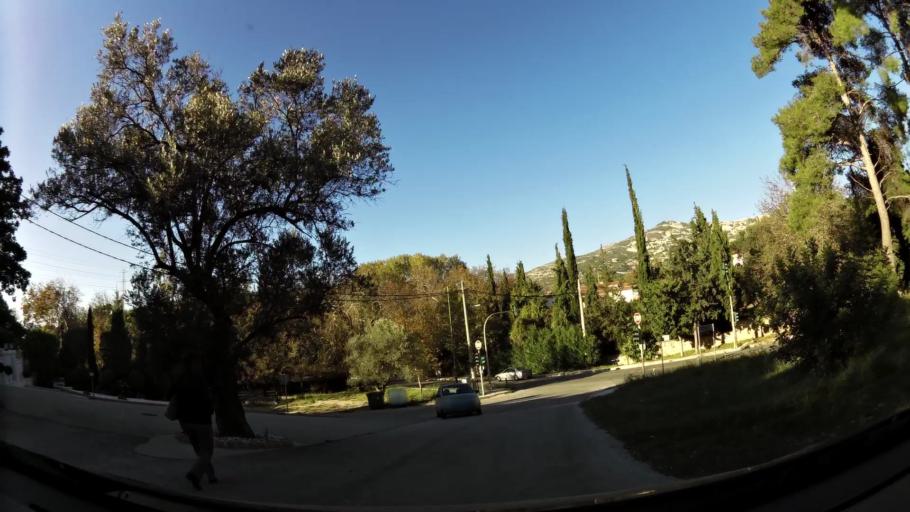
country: GR
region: Attica
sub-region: Nomarchia Athinas
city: Penteli
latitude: 38.0512
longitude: 23.8664
